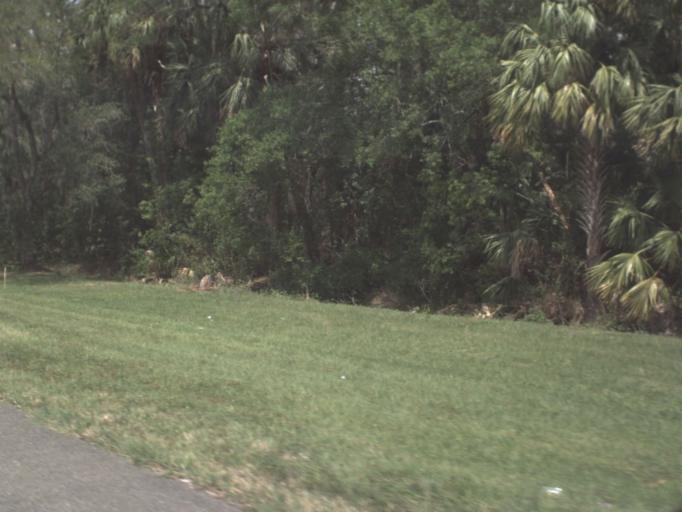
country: US
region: Florida
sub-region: Flagler County
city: Bunnell
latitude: 29.3327
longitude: -81.3106
